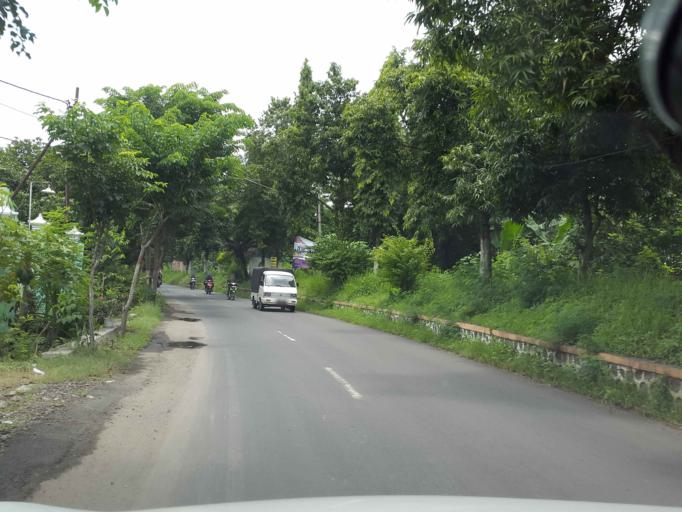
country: ID
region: East Java
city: Mojokerto
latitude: -7.4578
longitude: 112.4213
